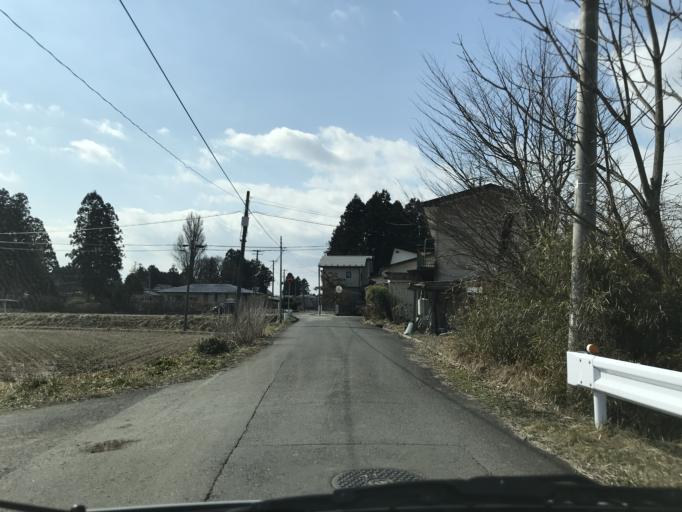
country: JP
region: Iwate
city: Mizusawa
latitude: 39.0430
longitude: 141.1410
